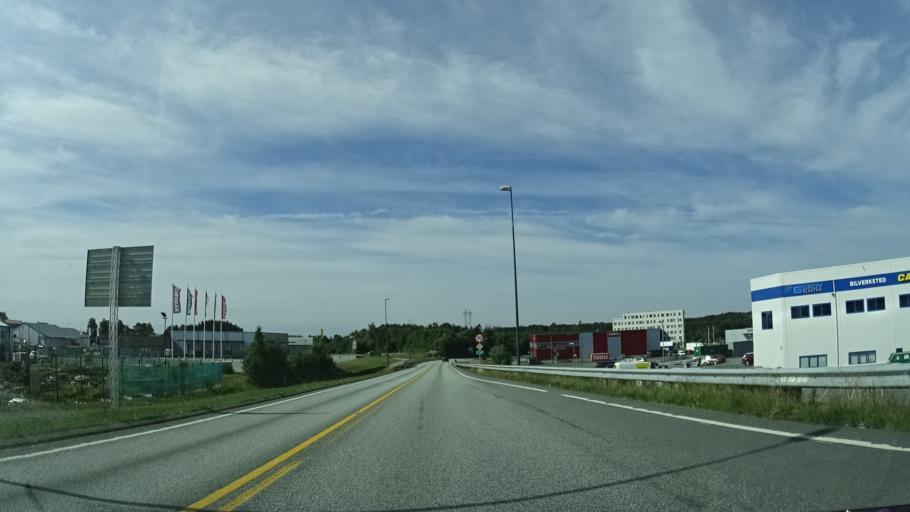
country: NO
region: Hordaland
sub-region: Stord
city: Leirvik
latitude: 59.7619
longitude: 5.4506
